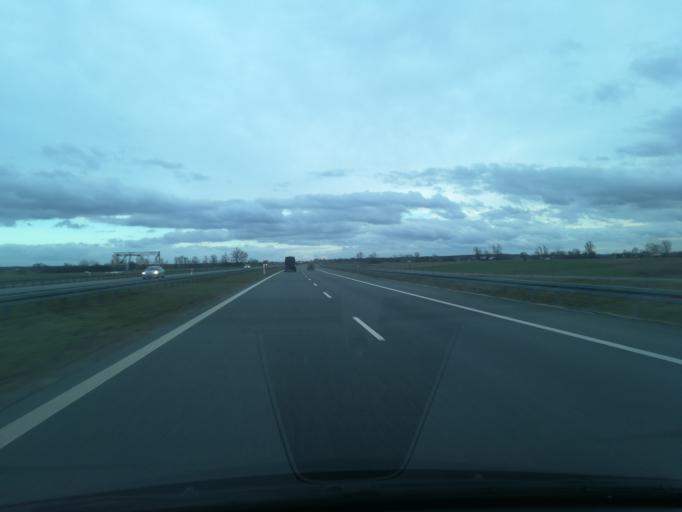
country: PL
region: Lodz Voivodeship
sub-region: Powiat kutnowski
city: Lanieta
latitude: 52.3961
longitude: 19.2859
